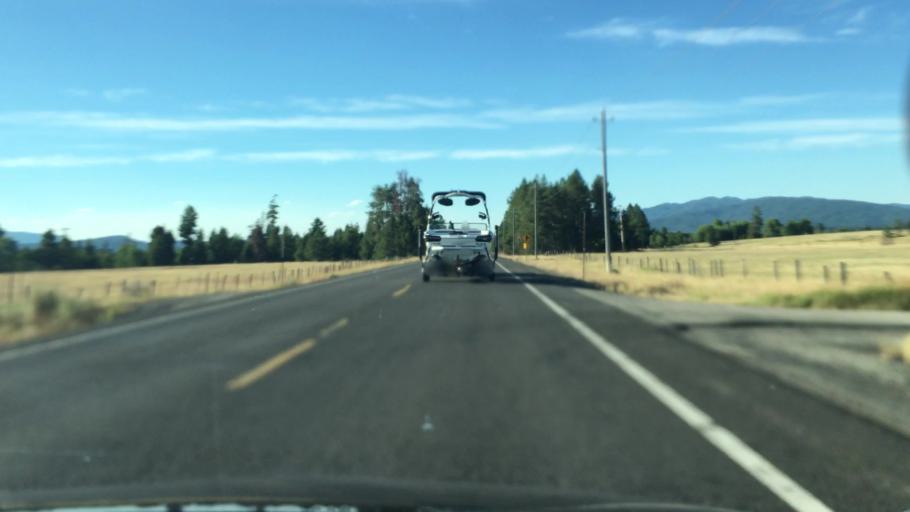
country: US
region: Idaho
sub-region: Valley County
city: Cascade
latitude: 44.4522
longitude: -115.9994
